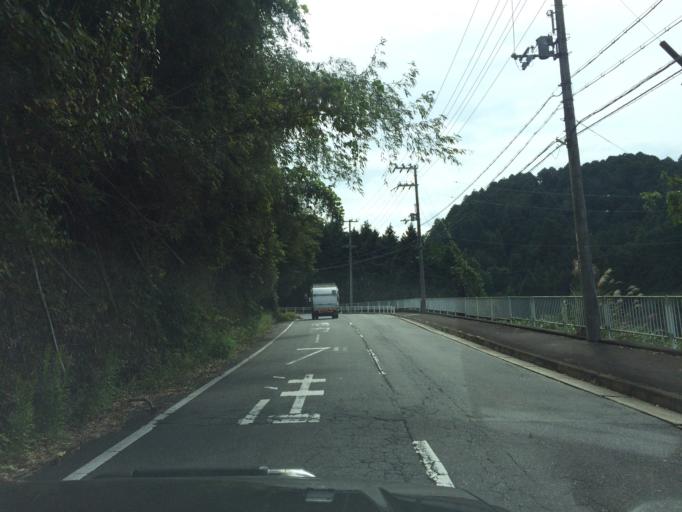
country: JP
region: Mie
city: Nabari
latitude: 34.6778
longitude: 135.9809
